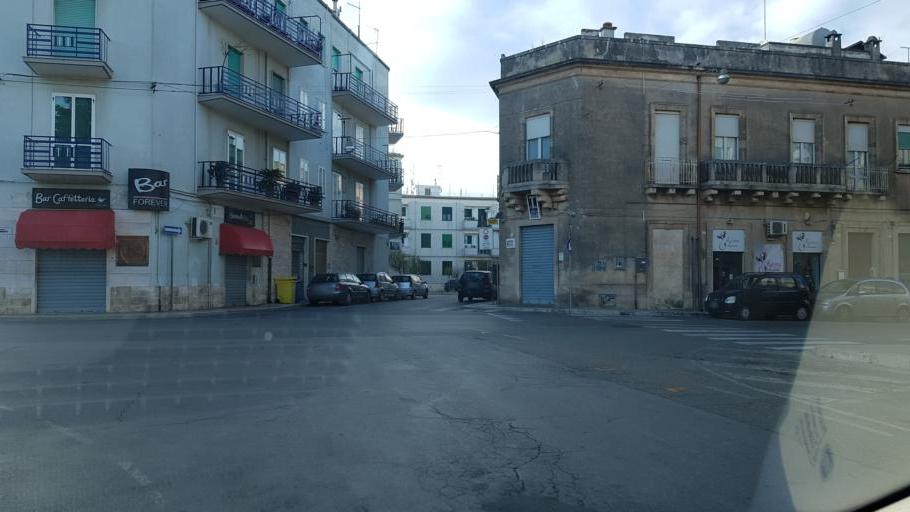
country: IT
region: Apulia
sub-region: Provincia di Taranto
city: Martina Franca
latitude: 40.7018
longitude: 17.3437
